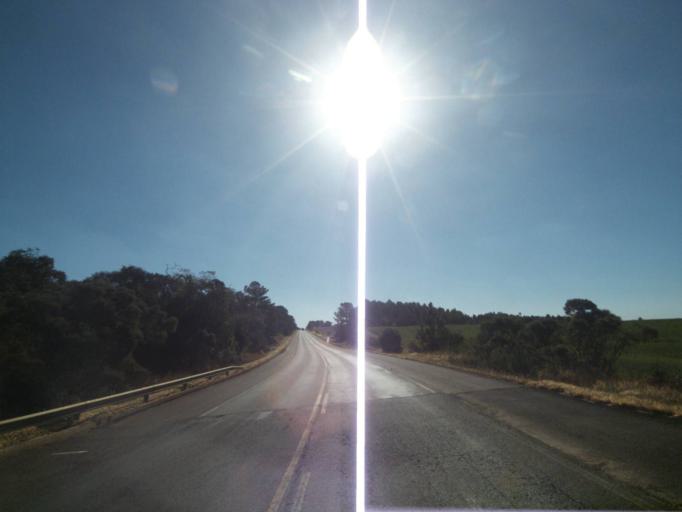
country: BR
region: Parana
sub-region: Tibagi
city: Tibagi
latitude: -24.6799
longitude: -50.4454
